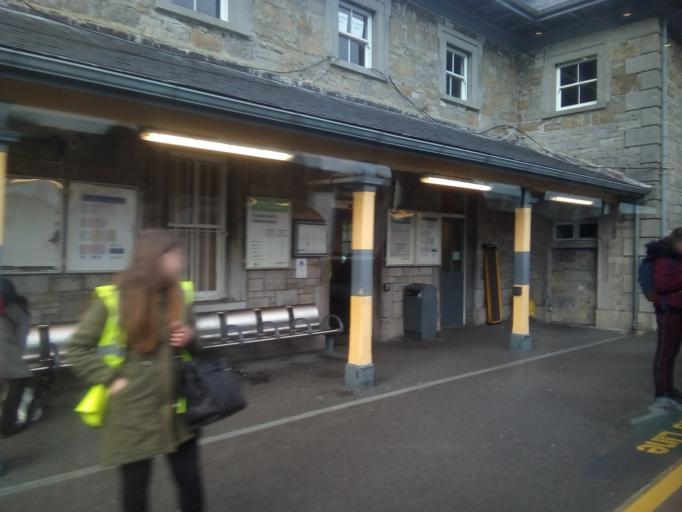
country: IE
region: Leinster
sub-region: An Longfort
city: Longford
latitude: 53.7243
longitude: -7.7962
